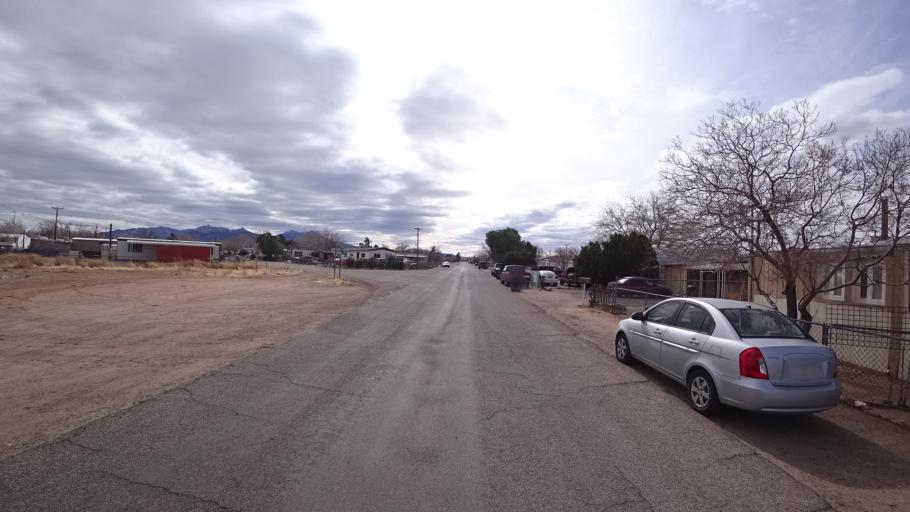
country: US
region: Arizona
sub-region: Mohave County
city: New Kingman-Butler
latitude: 35.2466
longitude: -113.9933
